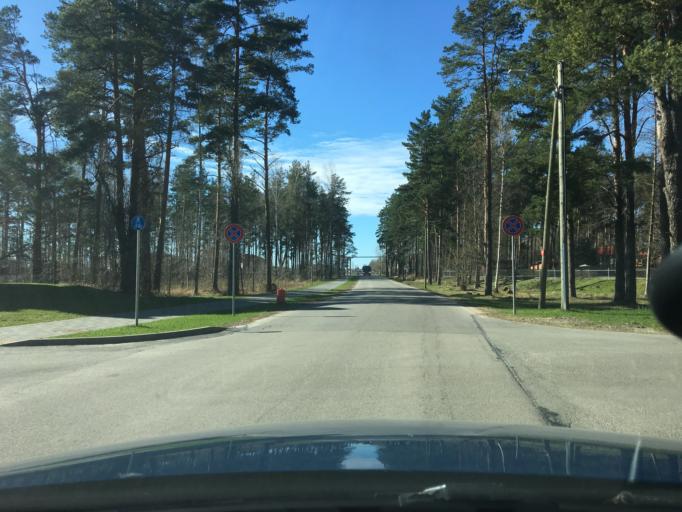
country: LV
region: Salaspils
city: Salaspils
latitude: 56.8709
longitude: 24.3439
